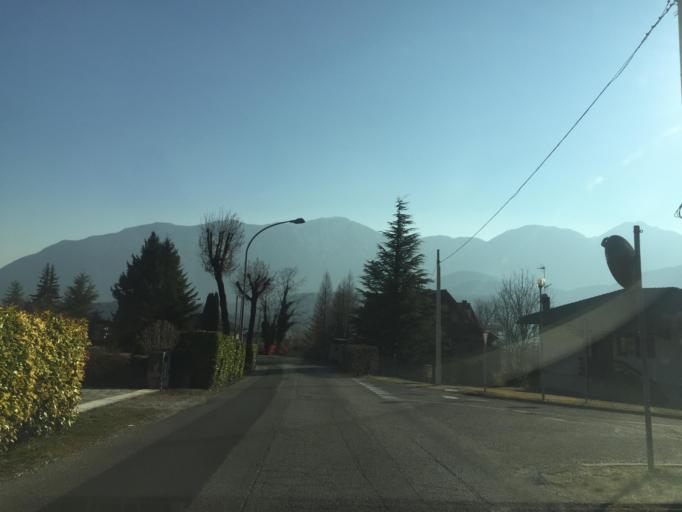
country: IT
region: Friuli Venezia Giulia
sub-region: Provincia di Udine
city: Tolmezzo
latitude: 46.4006
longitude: 13.0358
